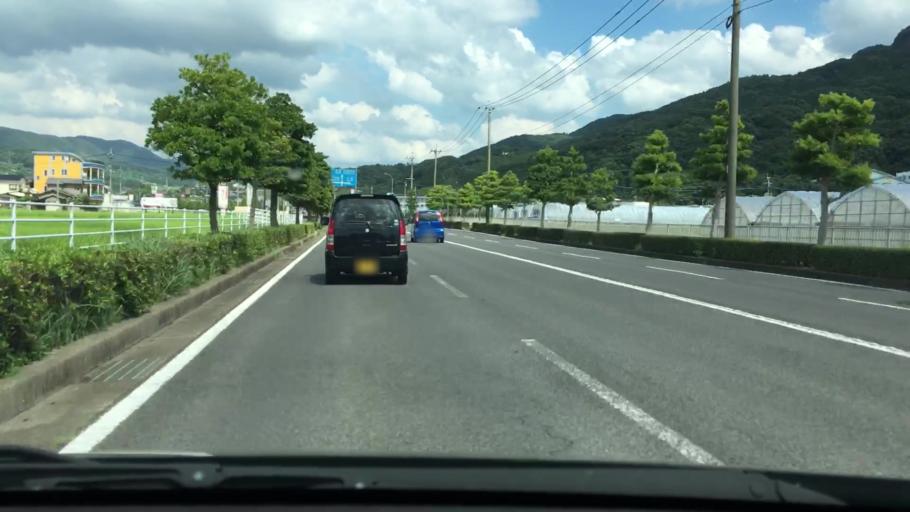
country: JP
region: Nagasaki
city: Sasebo
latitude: 33.2061
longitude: 129.6855
